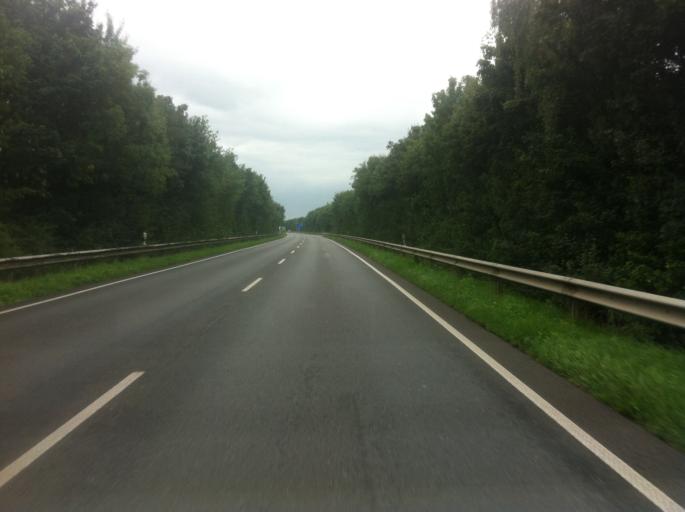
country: DE
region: North Rhine-Westphalia
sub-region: Regierungsbezirk Dusseldorf
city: Goch
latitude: 51.6766
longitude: 6.1217
